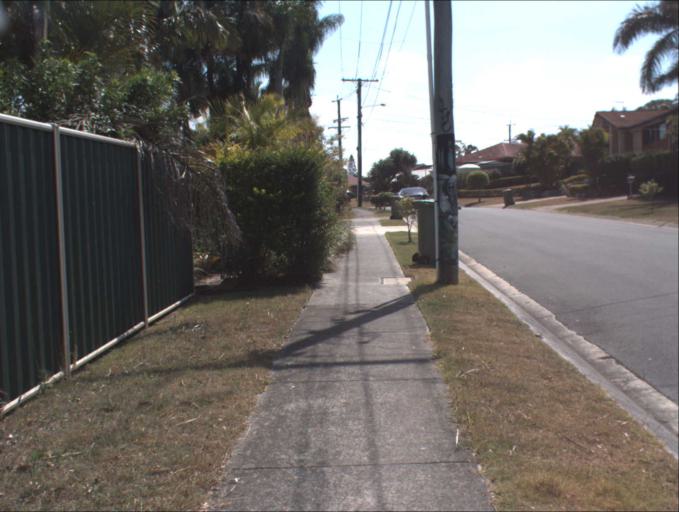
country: AU
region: Queensland
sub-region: Logan
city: Slacks Creek
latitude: -27.6606
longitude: 153.1845
